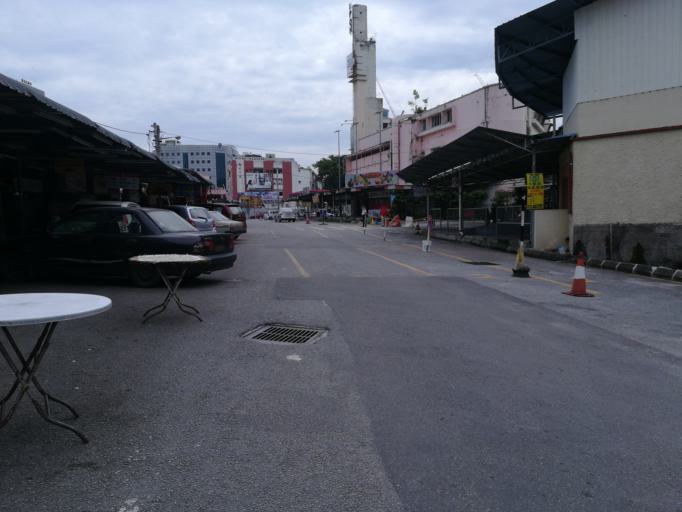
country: MY
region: Perak
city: Ipoh
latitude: 4.5951
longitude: 101.0873
